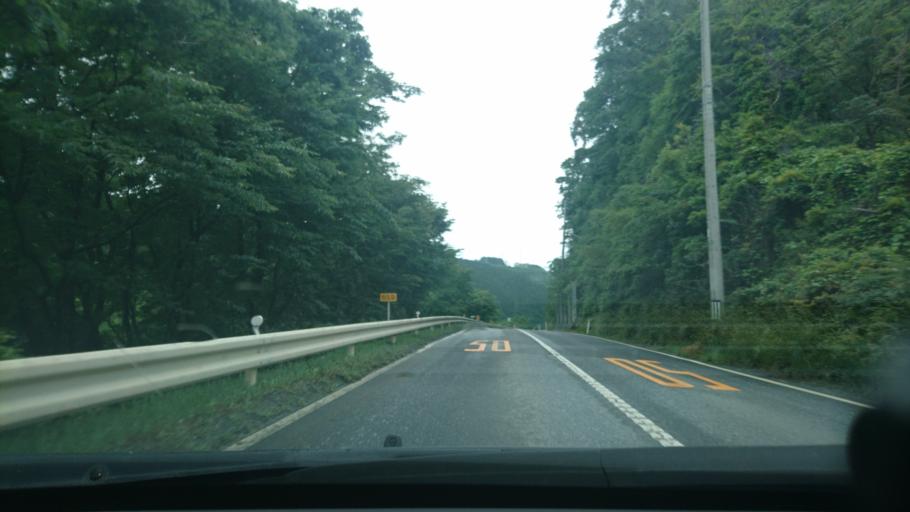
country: JP
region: Miyagi
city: Ishinomaki
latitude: 38.5407
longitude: 141.3041
